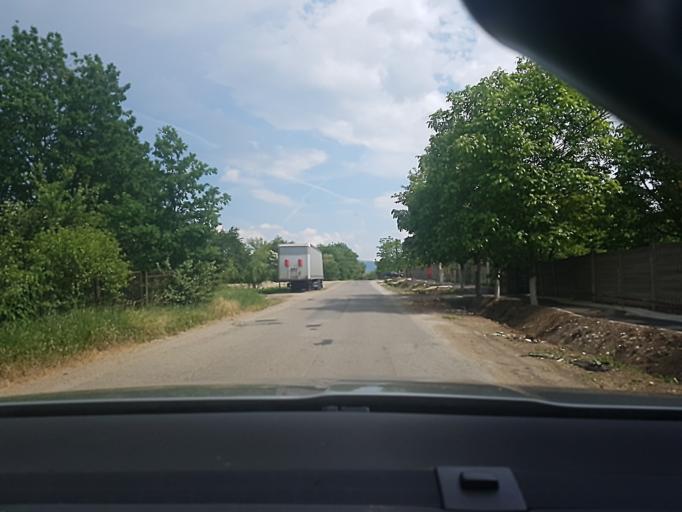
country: RO
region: Hunedoara
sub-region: Comuna Calan
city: Calan
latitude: 45.7229
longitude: 23.0228
